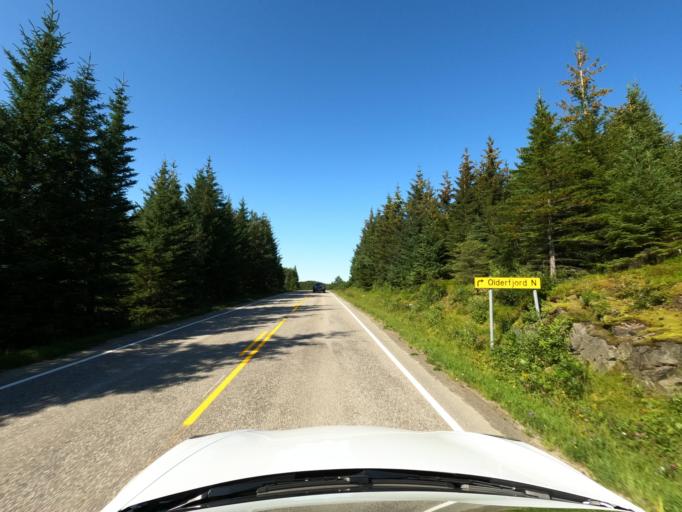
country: NO
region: Nordland
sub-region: Vagan
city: Kabelvag
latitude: 68.2478
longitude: 14.2808
